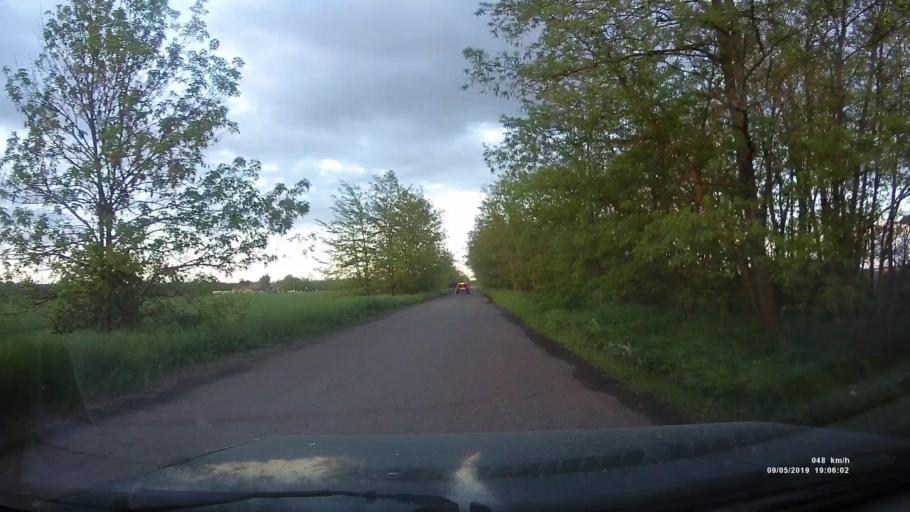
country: RU
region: Krasnodarskiy
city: Kanelovskaya
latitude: 46.7384
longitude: 39.1868
